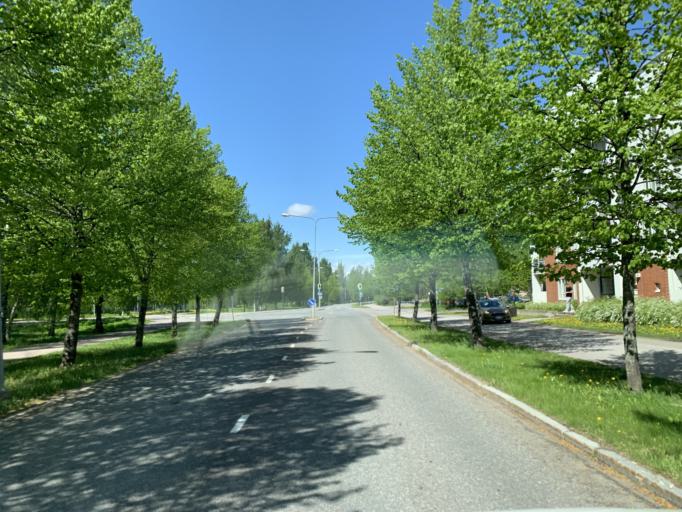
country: FI
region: Uusimaa
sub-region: Helsinki
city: Vantaa
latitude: 60.2484
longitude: 24.9991
